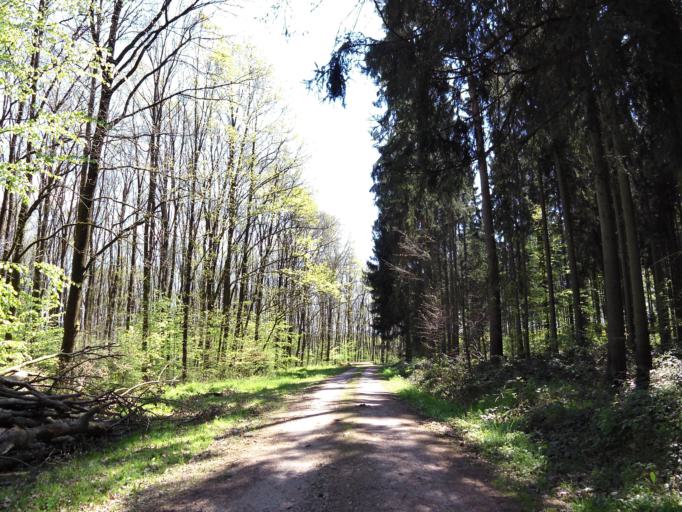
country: DE
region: Thuringia
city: Marksuhl
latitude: 50.8800
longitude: 10.2114
